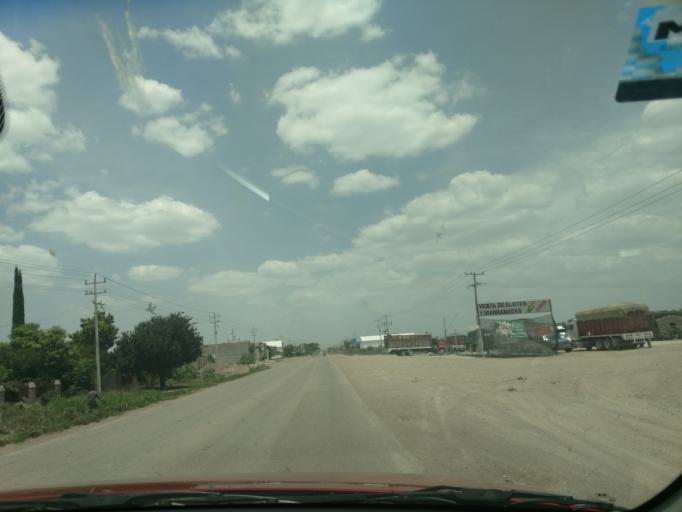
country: MX
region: San Luis Potosi
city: Ciudad Fernandez
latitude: 21.9459
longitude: -100.0520
